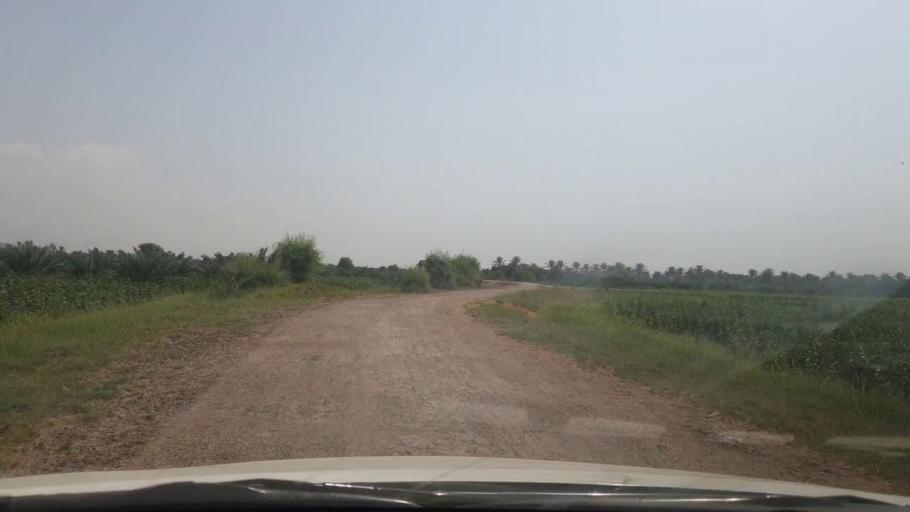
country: PK
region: Sindh
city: Khairpur
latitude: 27.5596
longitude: 68.8398
